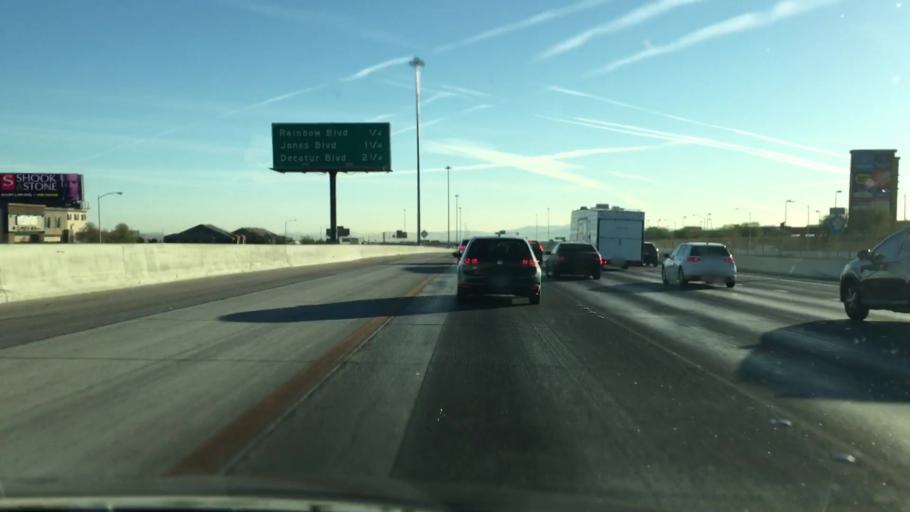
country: US
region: Nevada
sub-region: Clark County
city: Enterprise
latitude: 36.0663
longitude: -115.2520
